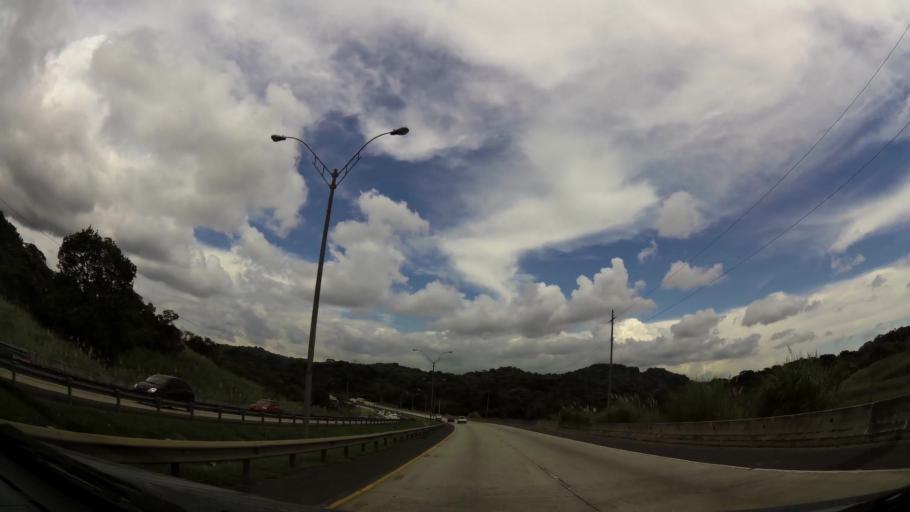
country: PA
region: Panama
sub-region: Distrito Arraijan
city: Arraijan
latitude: 8.9687
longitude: -79.6444
